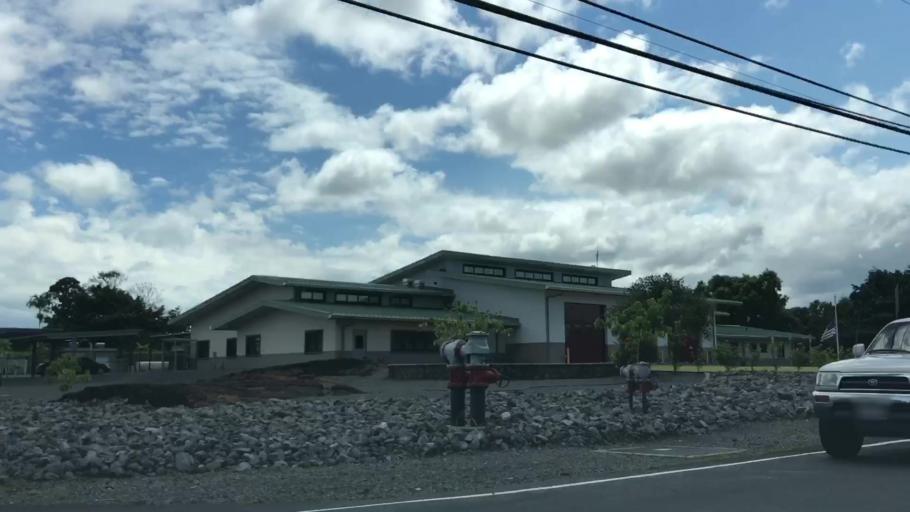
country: US
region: Hawaii
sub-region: Hawaii County
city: Hilo
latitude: 19.6739
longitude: -155.0776
